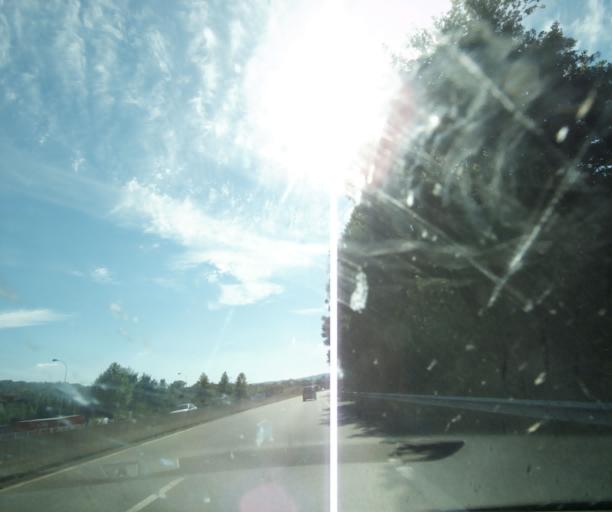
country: FR
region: Limousin
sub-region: Departement de la Correze
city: Ussac
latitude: 45.1774
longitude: 1.4903
